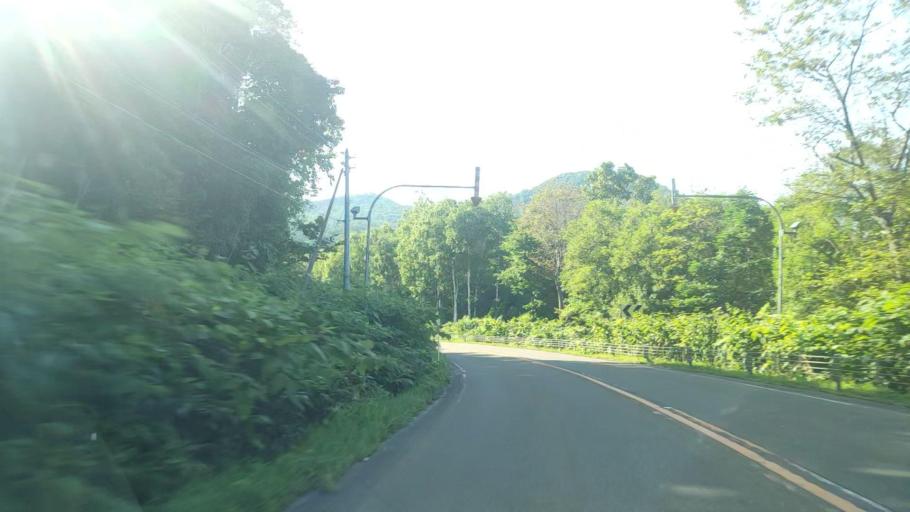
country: JP
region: Hokkaido
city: Nayoro
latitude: 44.7382
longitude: 142.1874
